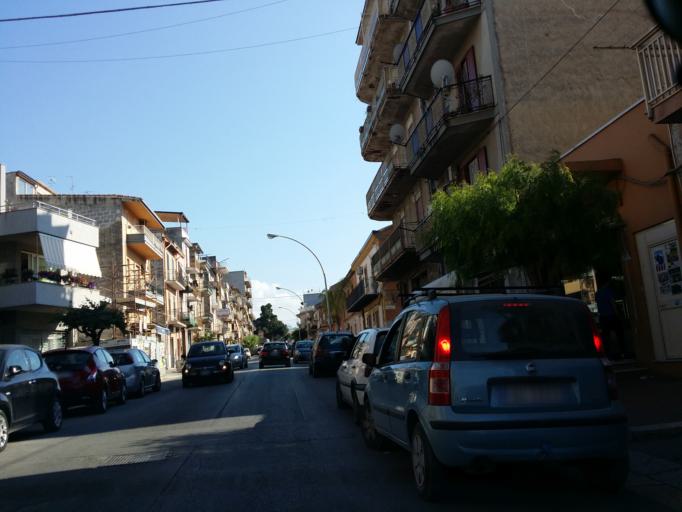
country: IT
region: Sicily
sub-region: Palermo
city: Misilmeri
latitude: 38.0280
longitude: 13.4481
